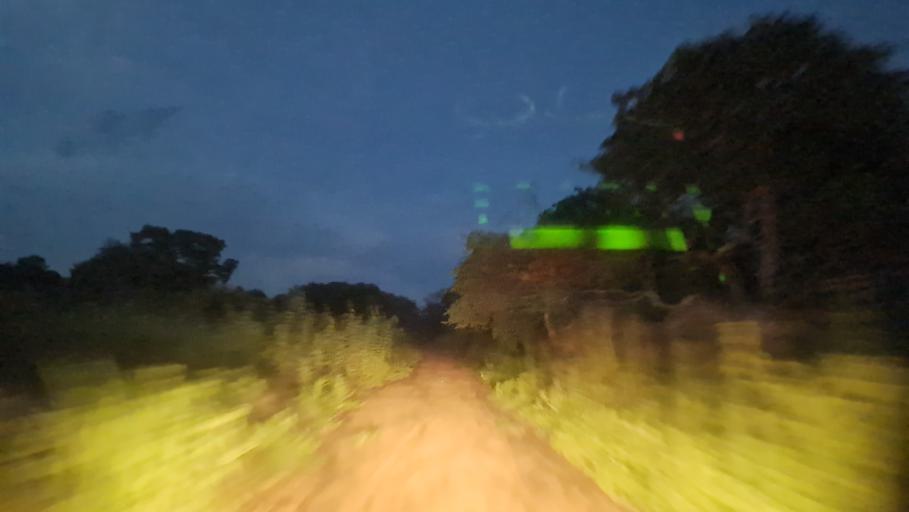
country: MZ
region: Nampula
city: Nampula
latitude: -14.6747
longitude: 39.8317
